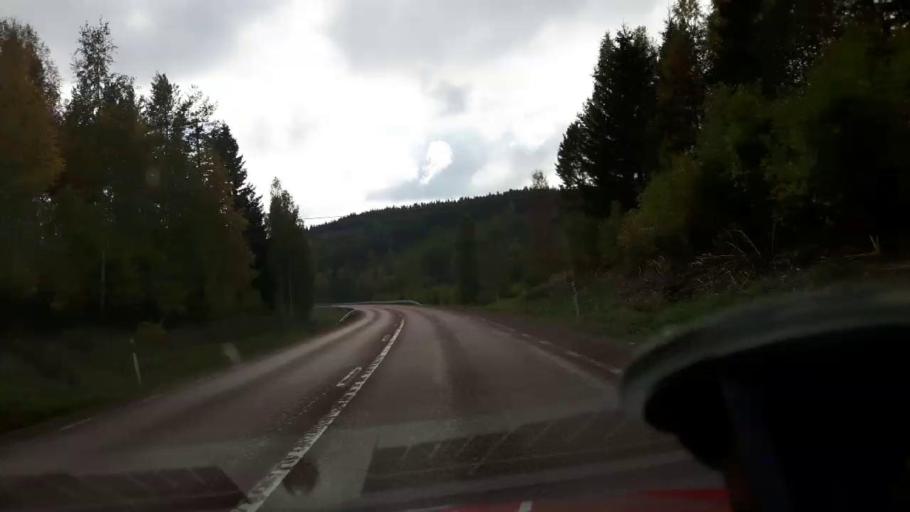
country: SE
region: Gaevleborg
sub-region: Bollnas Kommun
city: Arbra
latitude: 61.5989
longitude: 16.2964
